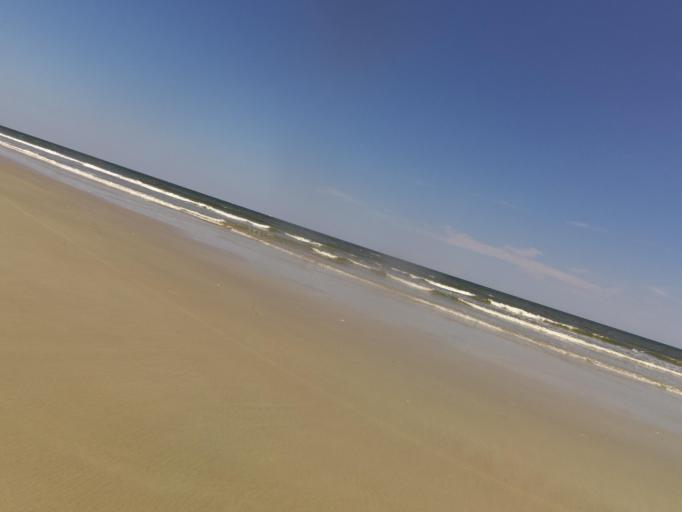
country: US
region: Florida
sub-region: Nassau County
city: Fernandina Beach
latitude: 30.6462
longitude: -81.4335
